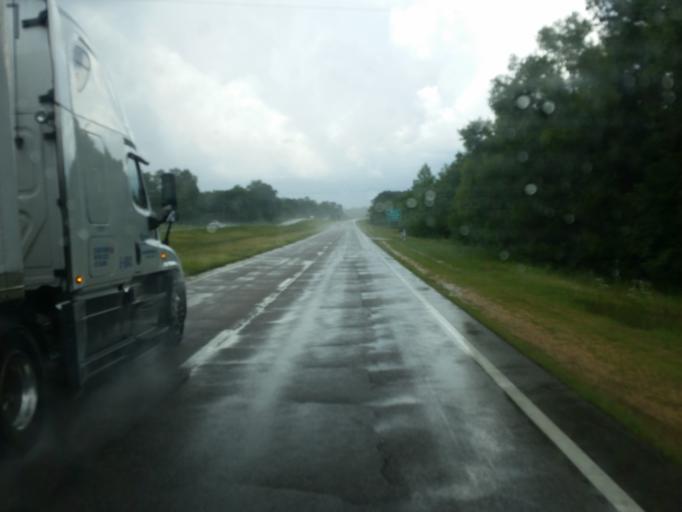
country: US
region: Mississippi
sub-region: George County
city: Lucedale
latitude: 30.9024
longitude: -88.4653
